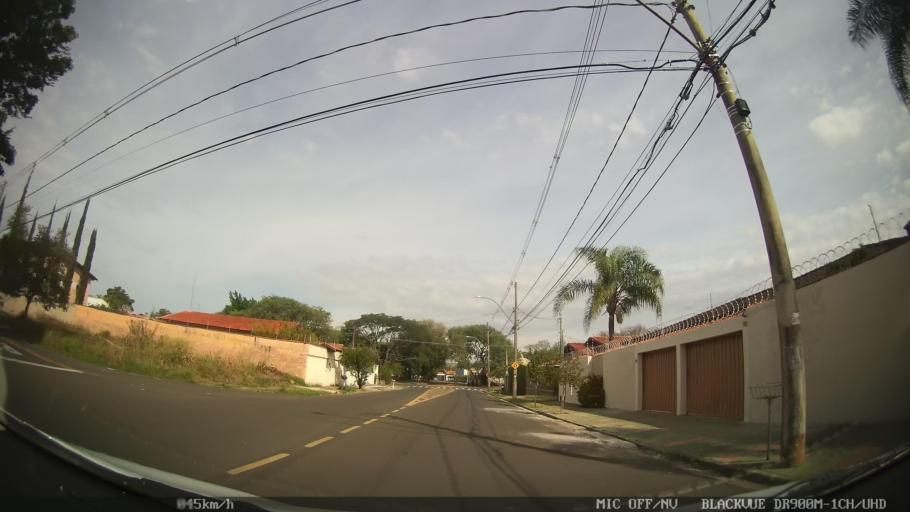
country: BR
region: Sao Paulo
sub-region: Piracicaba
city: Piracicaba
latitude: -22.7117
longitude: -47.6732
